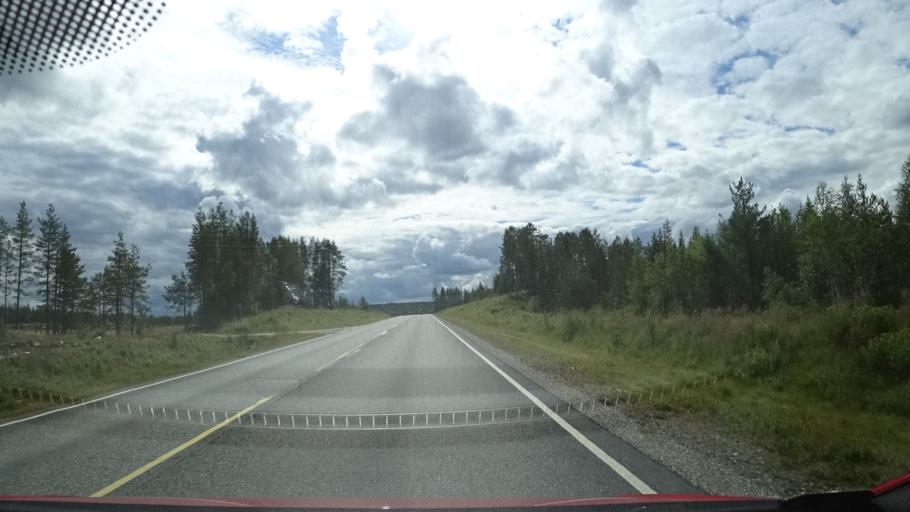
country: FI
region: Lapland
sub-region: Tunturi-Lappi
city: Kittilae
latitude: 67.4987
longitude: 24.8986
